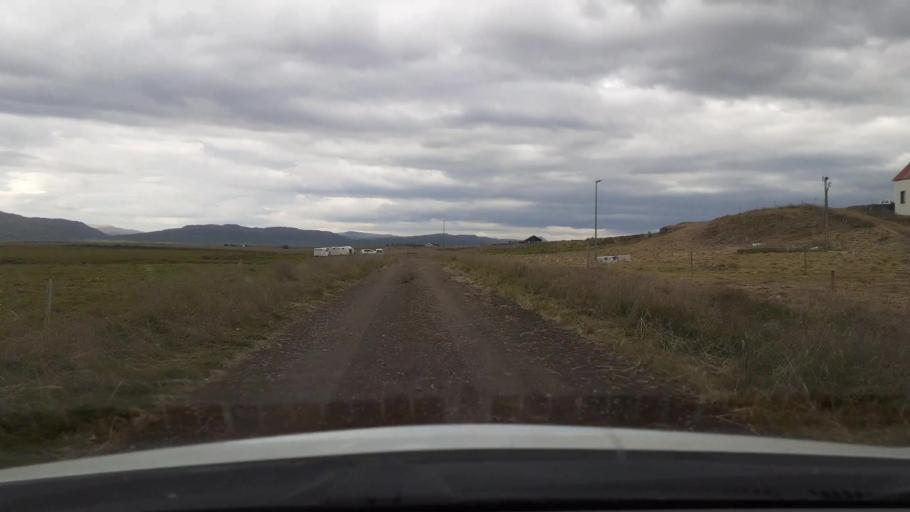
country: IS
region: West
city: Borgarnes
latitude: 64.6525
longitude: -21.8809
